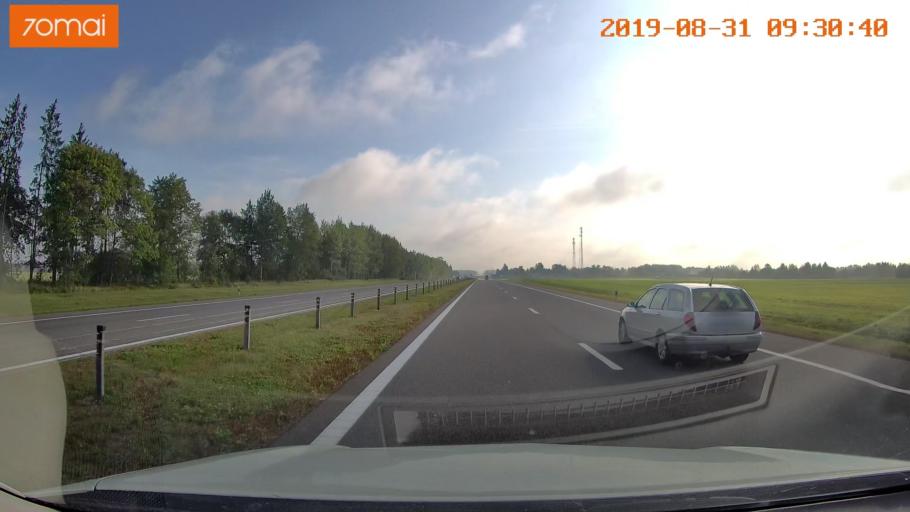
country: BY
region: Minsk
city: Byerazino
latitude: 53.8561
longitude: 29.1344
